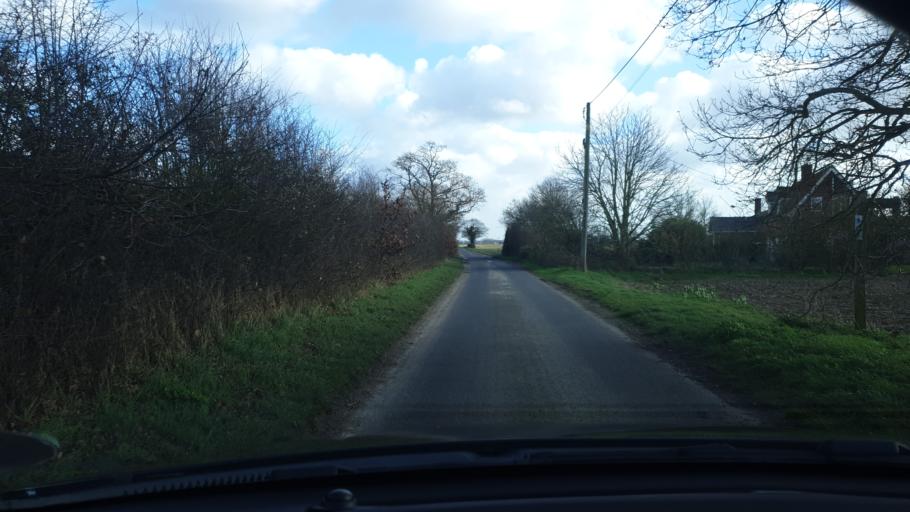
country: GB
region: England
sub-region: Essex
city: Manningtree
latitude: 51.9193
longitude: 1.0536
